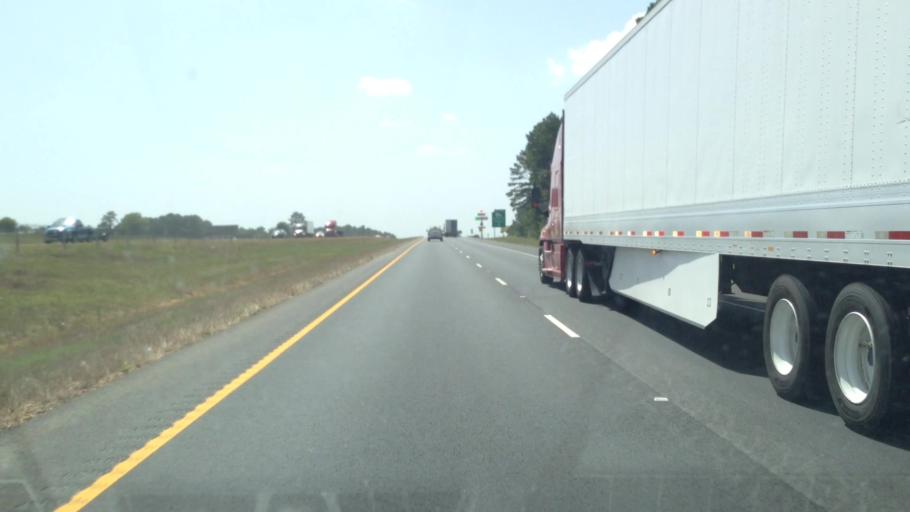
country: US
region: Louisiana
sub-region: Webster Parish
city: Minden
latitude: 32.5791
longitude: -93.2409
